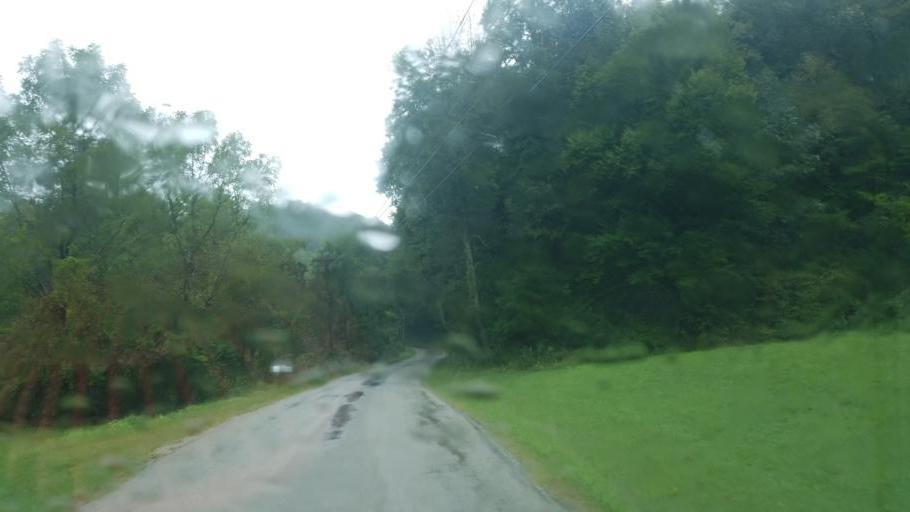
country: US
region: Ohio
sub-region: Adams County
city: Peebles
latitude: 38.8025
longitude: -83.2527
